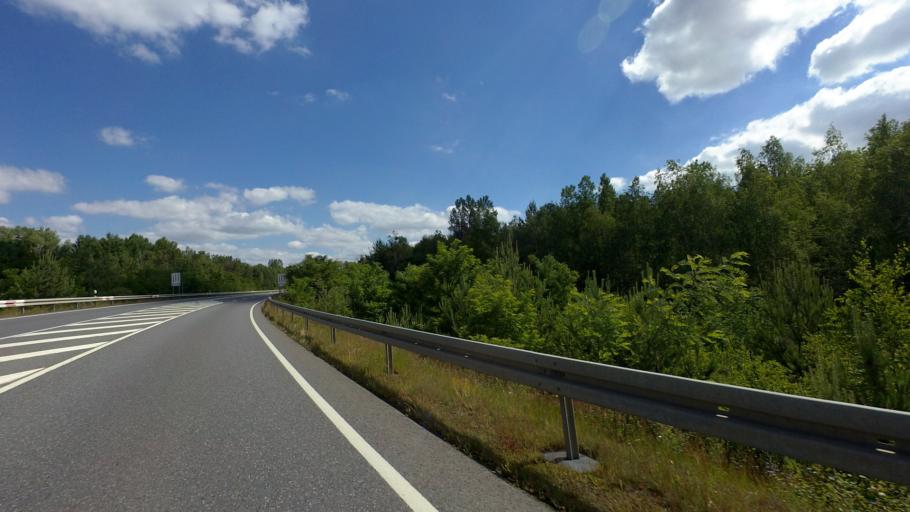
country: DE
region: Brandenburg
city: Senftenberg
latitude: 51.5333
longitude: 14.0234
